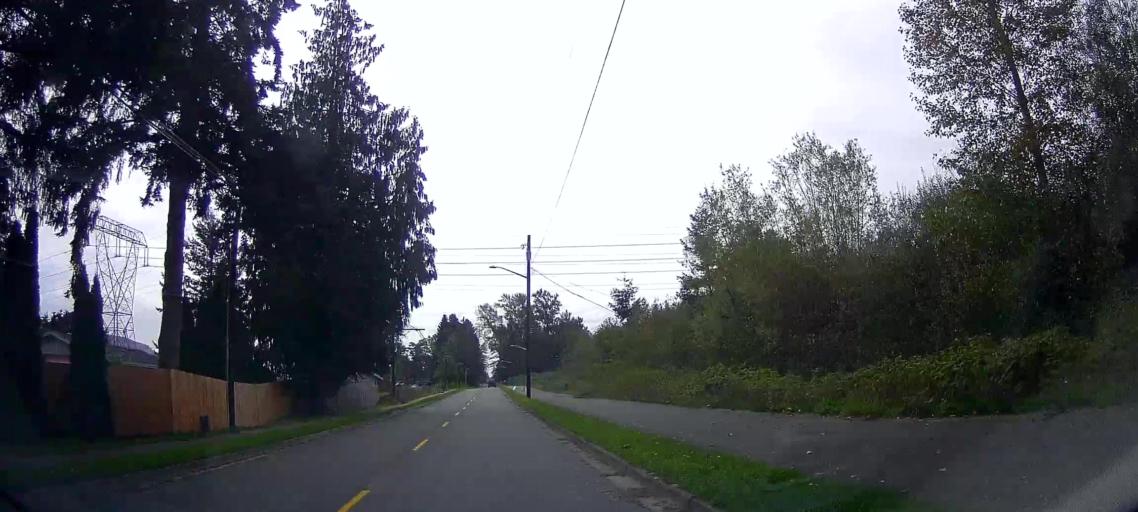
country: US
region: Washington
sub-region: Skagit County
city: Sedro-Woolley
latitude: 48.5207
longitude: -122.2134
